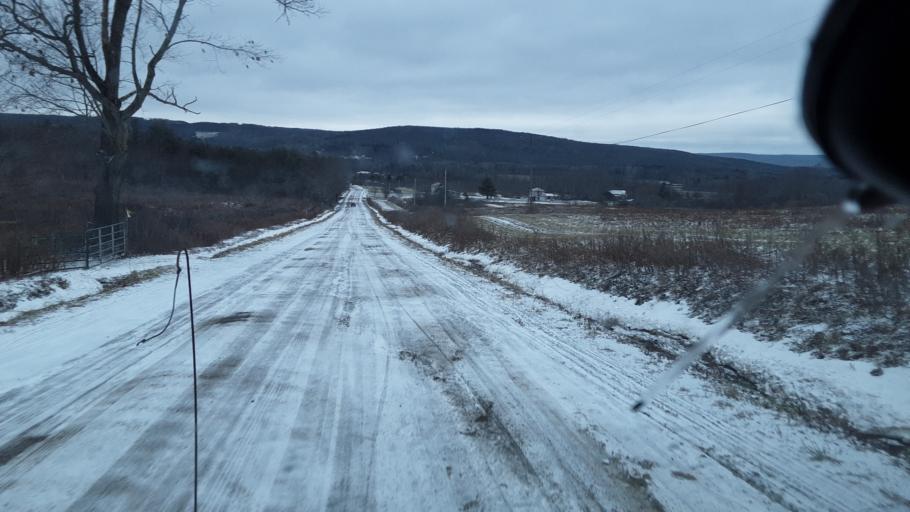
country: US
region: New York
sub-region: Allegany County
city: Friendship
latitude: 42.2889
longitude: -78.1624
